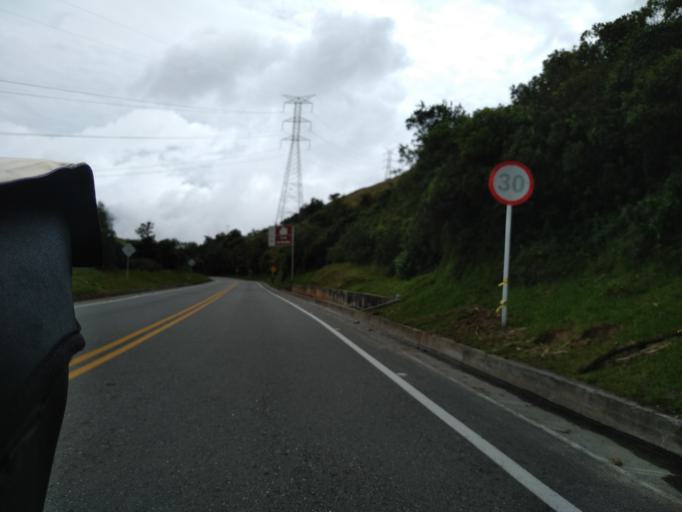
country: CO
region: Caldas
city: Villamaria
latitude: 5.0157
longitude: -75.3406
